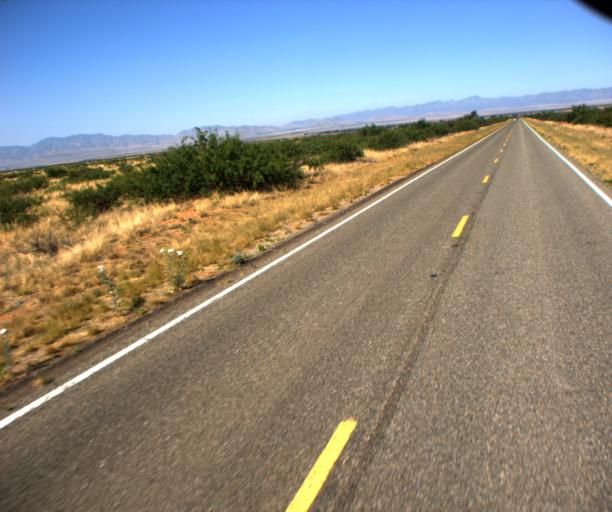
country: US
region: Arizona
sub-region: Graham County
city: Swift Trail Junction
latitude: 32.5852
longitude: -109.9314
